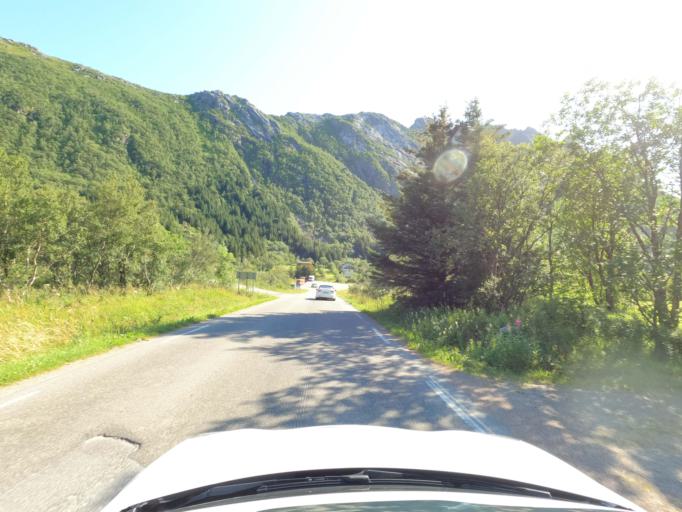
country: NO
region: Nordland
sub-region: Vagan
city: Kabelvag
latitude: 68.2056
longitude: 14.2401
